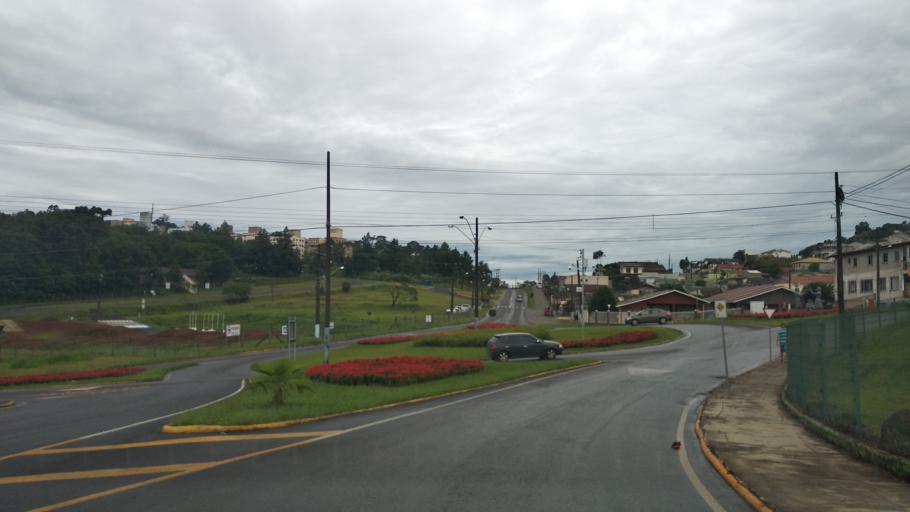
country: BR
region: Santa Catarina
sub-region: Videira
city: Videira
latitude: -26.9910
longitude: -51.1815
